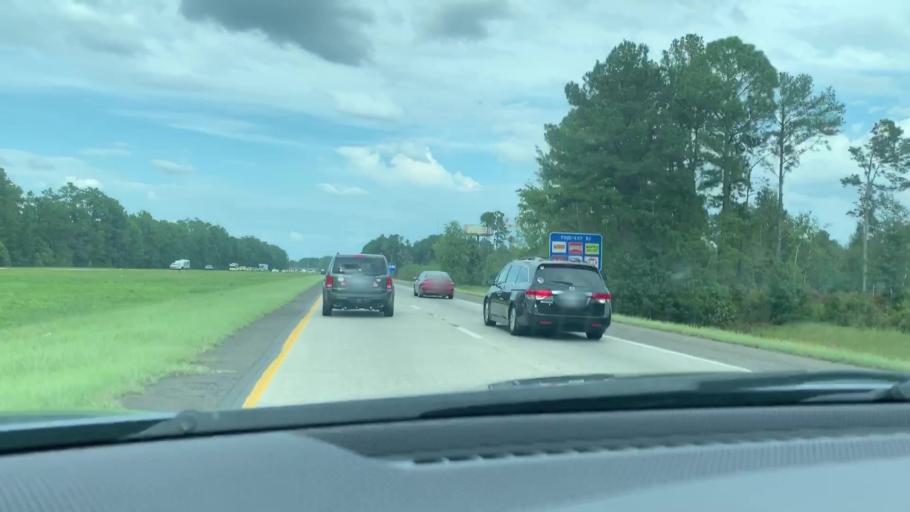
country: US
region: South Carolina
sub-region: Colleton County
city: Walterboro
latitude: 32.8680
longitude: -80.7225
